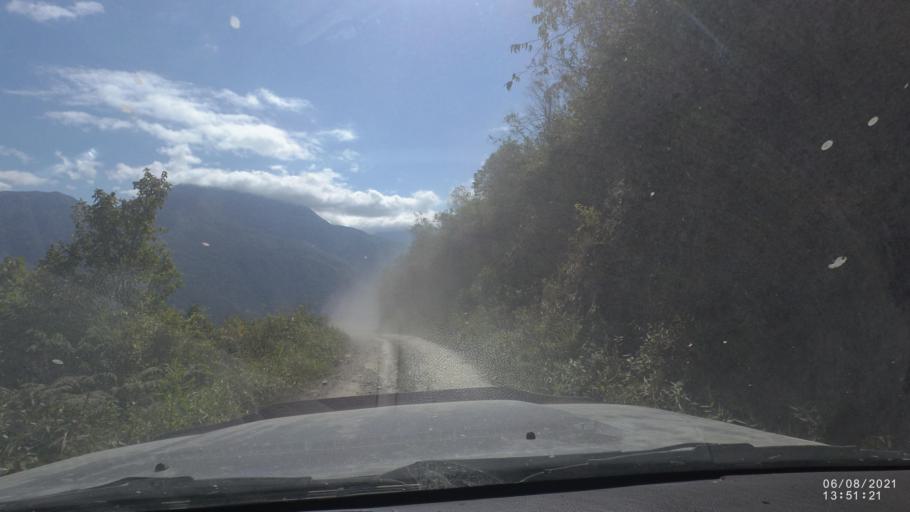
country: BO
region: La Paz
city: Quime
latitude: -16.6533
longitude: -66.7257
